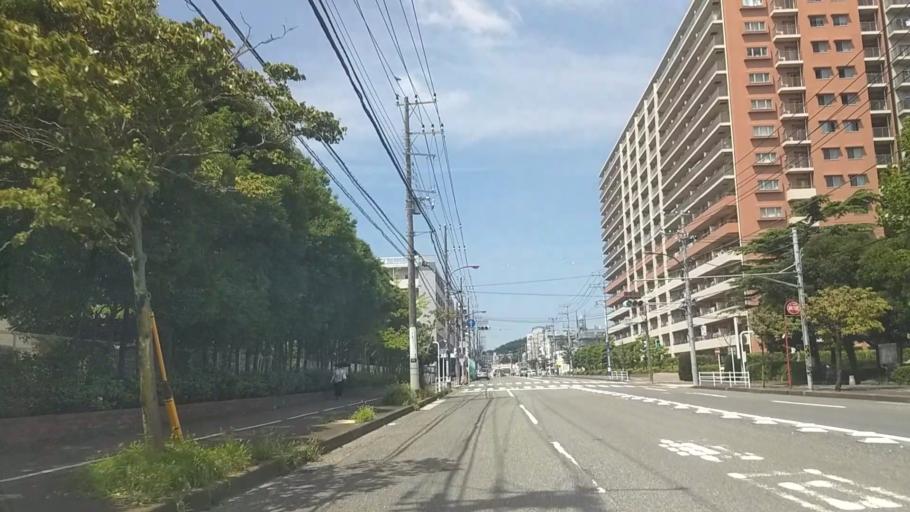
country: JP
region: Kanagawa
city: Yokosuka
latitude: 35.3170
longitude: 139.6348
